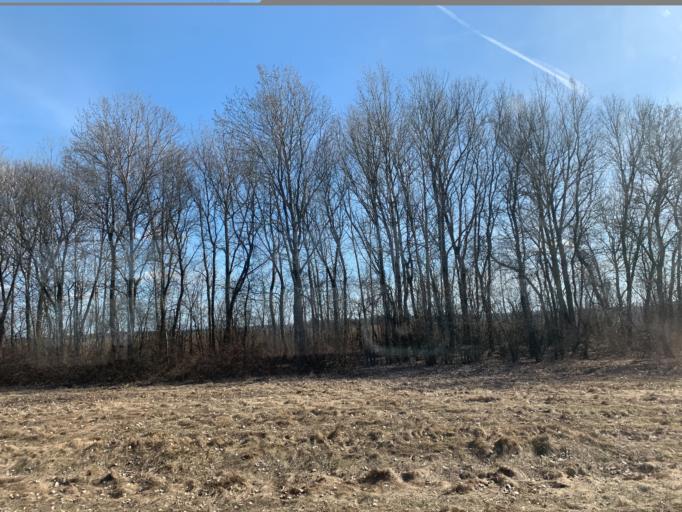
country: BY
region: Minsk
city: Haradzyeya
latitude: 53.3857
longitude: 26.5980
